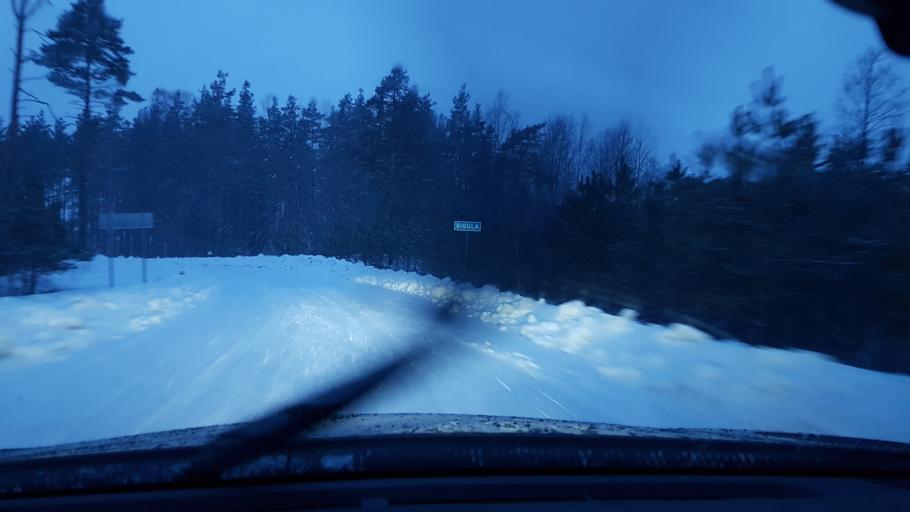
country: EE
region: Harju
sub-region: Kuusalu vald
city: Kuusalu
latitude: 59.4600
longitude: 25.5907
